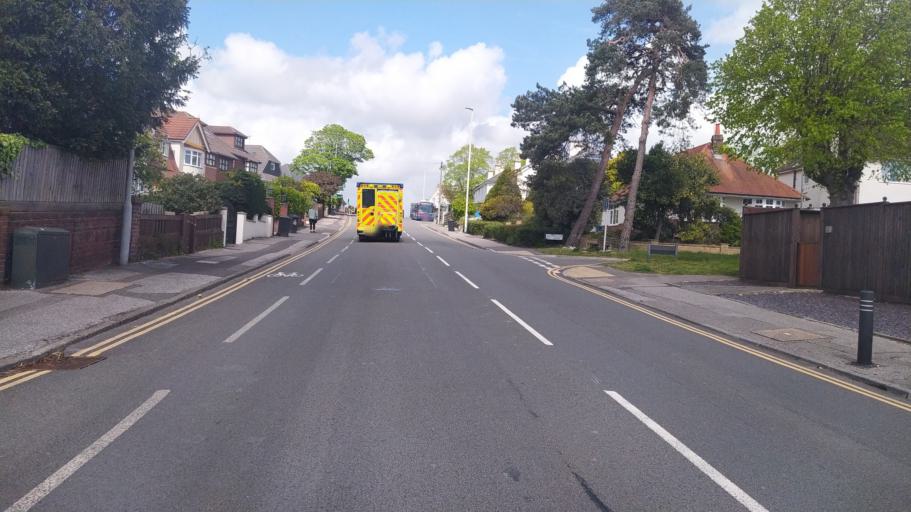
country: GB
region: England
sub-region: Dorset
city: Parkstone
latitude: 50.7244
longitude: -1.9650
